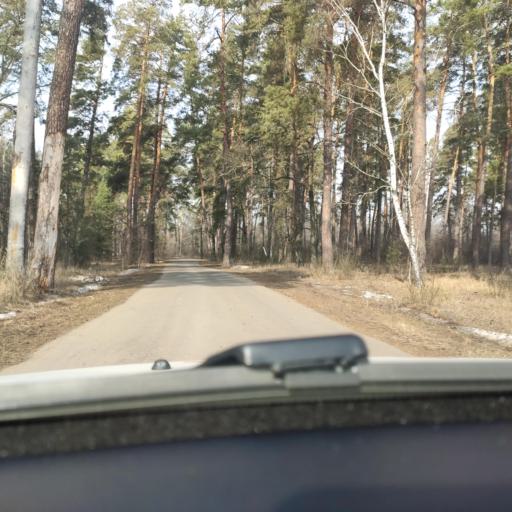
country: RU
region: Voronezj
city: Ramon'
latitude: 51.8909
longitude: 39.3673
